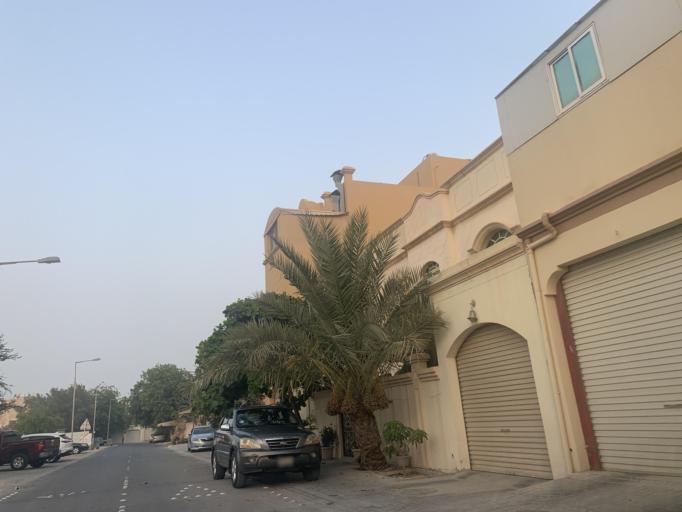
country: BH
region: Manama
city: Jidd Hafs
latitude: 26.2243
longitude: 50.5138
